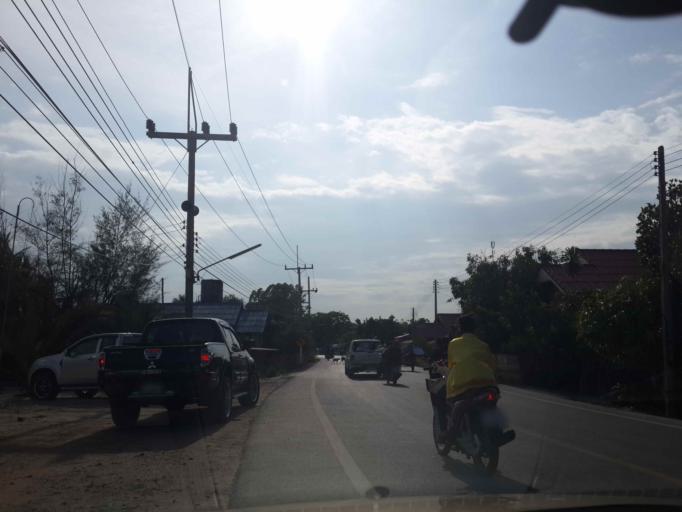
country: TH
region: Pattani
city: Yaring
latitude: 6.9287
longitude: 101.3207
